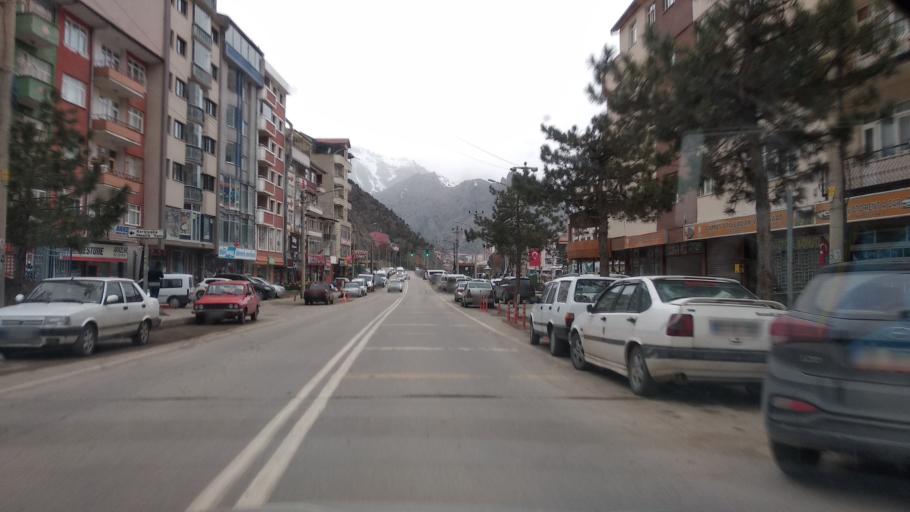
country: TR
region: Gumushane
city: Gumushkhane
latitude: 40.4575
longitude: 39.4803
